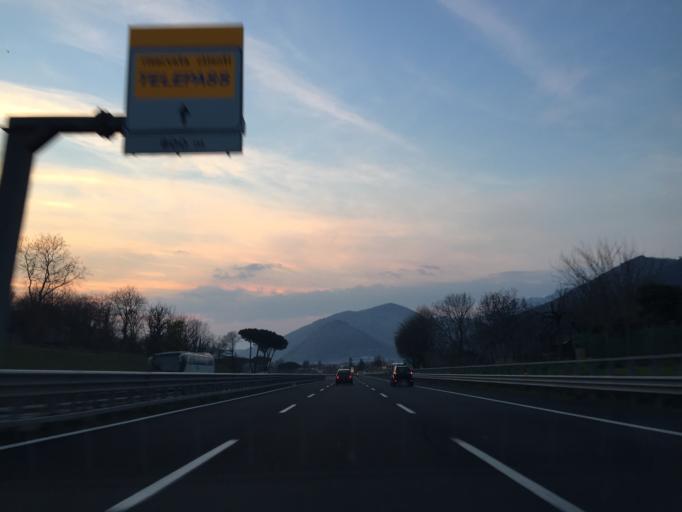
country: IT
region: Campania
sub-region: Provincia di Salerno
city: Piazza del Galdo-Sant'Angelo
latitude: 40.7717
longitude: 14.7360
